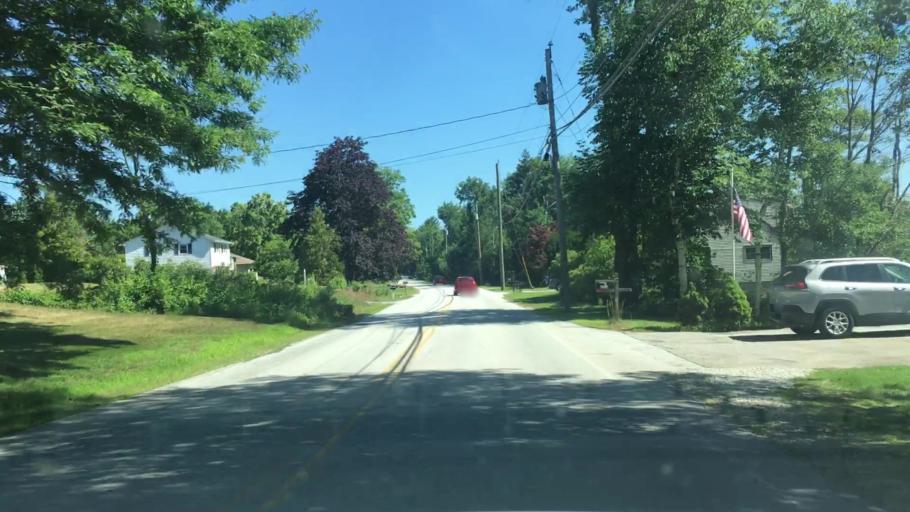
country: US
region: New Hampshire
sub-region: Rockingham County
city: Auburn
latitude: 43.0317
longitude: -71.3849
